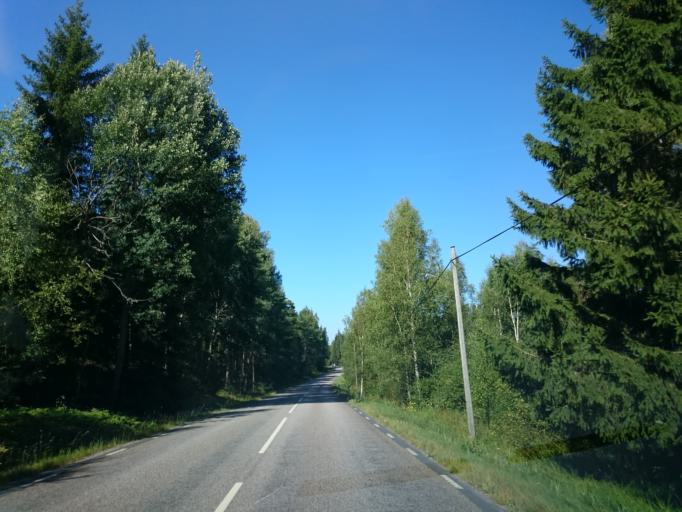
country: SE
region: OEstergoetland
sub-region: Norrkopings Kommun
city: Krokek
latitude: 58.6581
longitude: 16.5188
